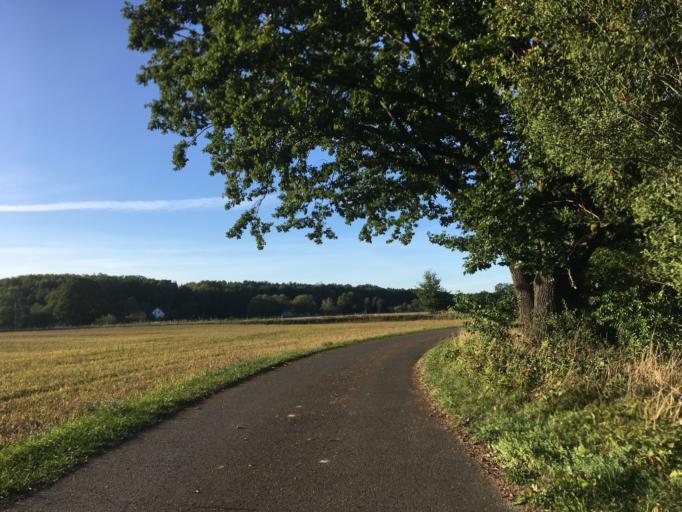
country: PL
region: Lubusz
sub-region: Powiat zarski
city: Trzebiel
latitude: 51.6358
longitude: 14.7537
